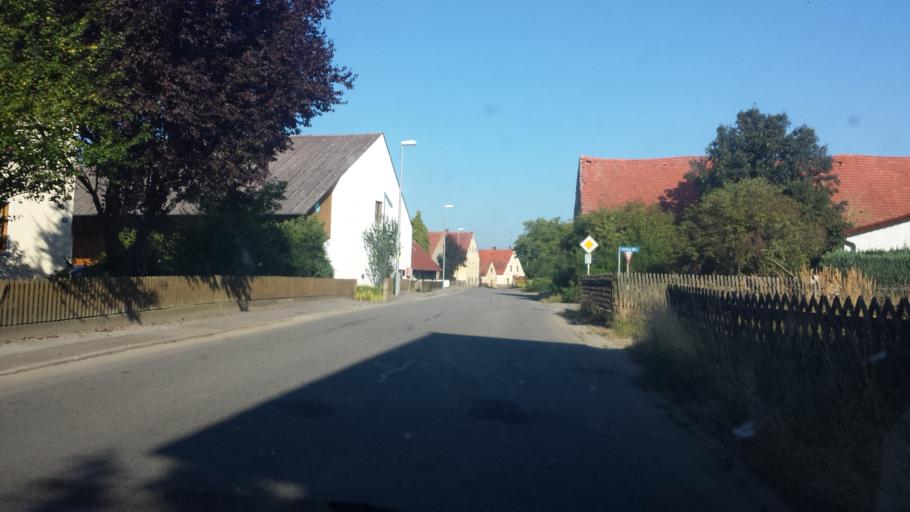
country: DE
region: Bavaria
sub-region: Lower Bavaria
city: Neustadt an der Donau
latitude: 48.8315
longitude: 11.7736
